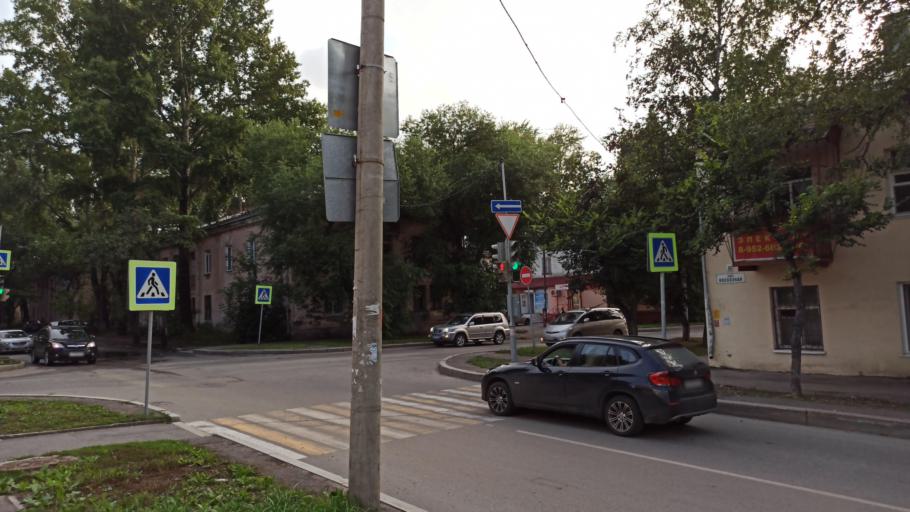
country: RU
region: Tomsk
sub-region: Tomskiy Rayon
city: Tomsk
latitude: 56.4808
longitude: 85.0032
